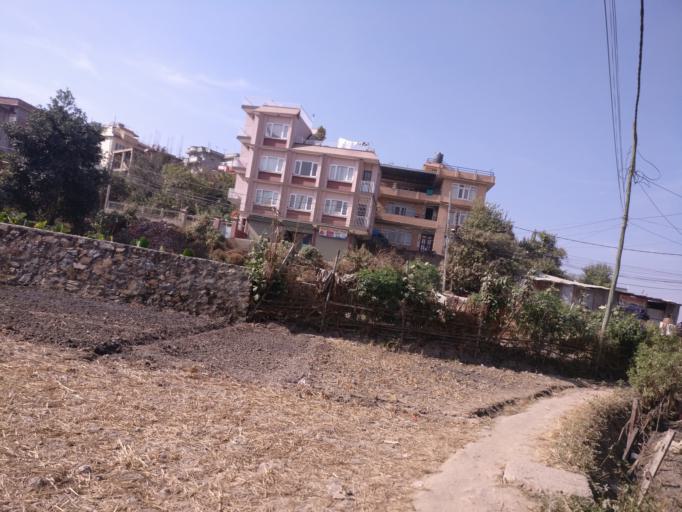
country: NP
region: Central Region
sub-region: Bagmati Zone
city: Patan
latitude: 27.6764
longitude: 85.3311
